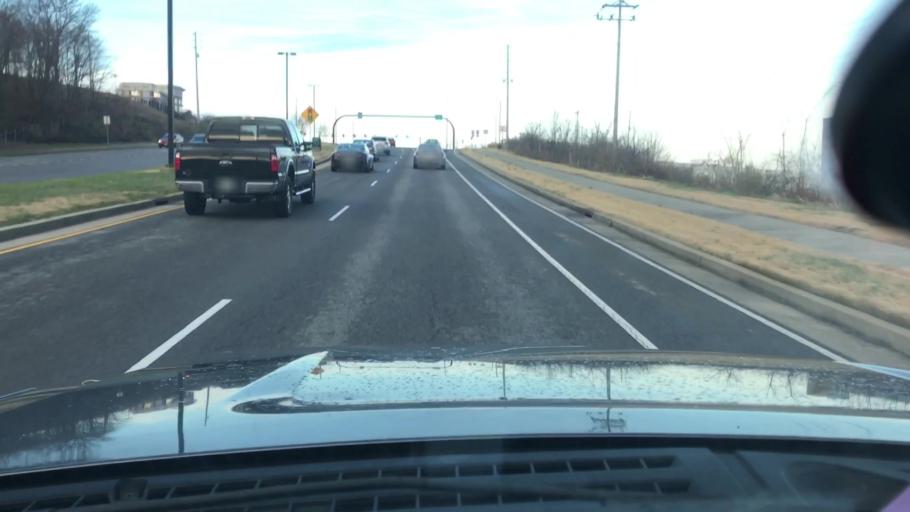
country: US
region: Tennessee
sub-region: Williamson County
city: Franklin
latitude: 35.9335
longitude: -86.8157
